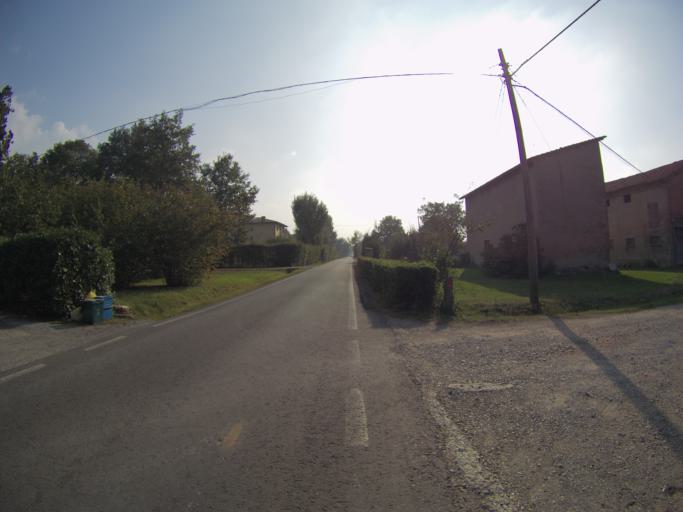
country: IT
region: Emilia-Romagna
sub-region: Provincia di Reggio Emilia
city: Forche
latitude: 44.6603
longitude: 10.5730
